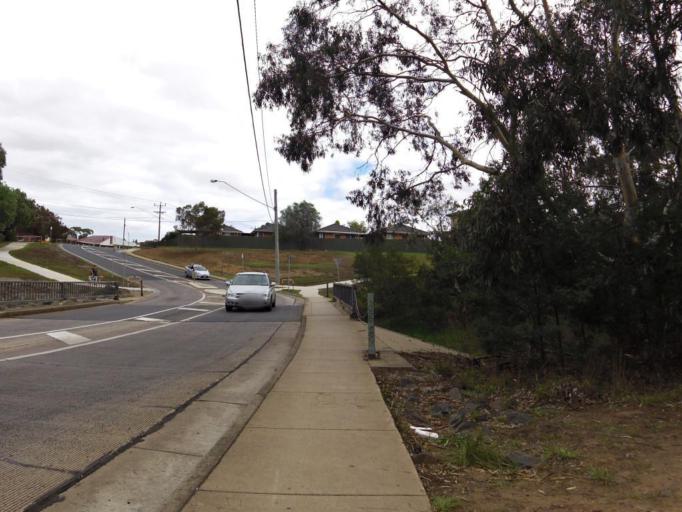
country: AU
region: Victoria
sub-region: Wyndham
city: Werribee
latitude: -37.8990
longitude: 144.6573
